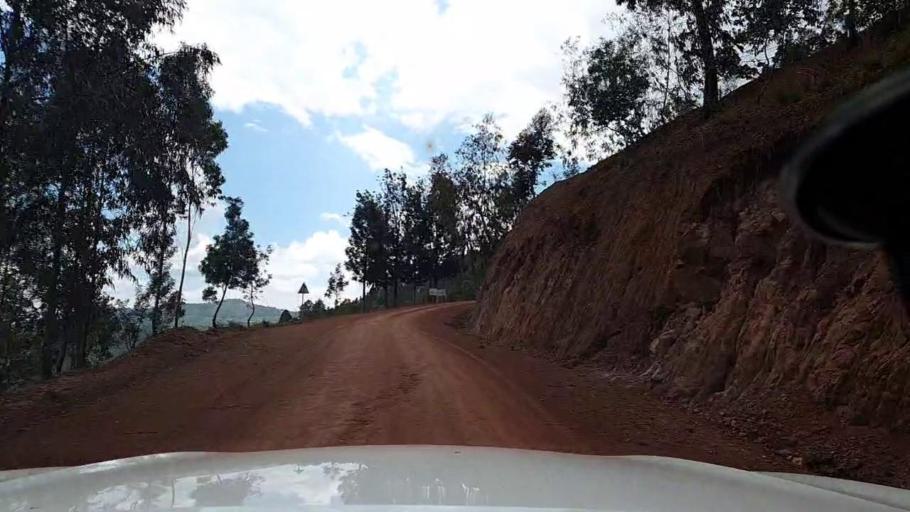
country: RW
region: Northern Province
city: Byumba
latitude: -1.7560
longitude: 29.8471
